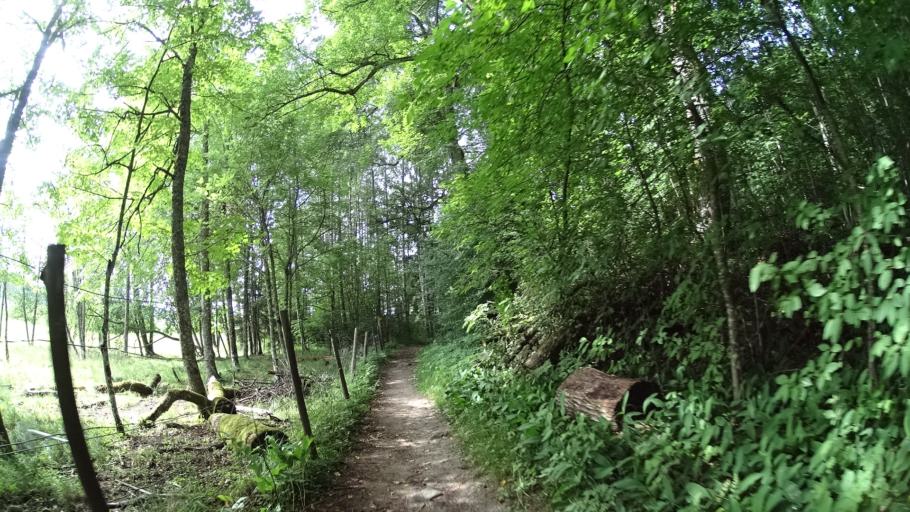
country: FI
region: Uusimaa
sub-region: Helsinki
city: Espoo
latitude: 60.1779
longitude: 24.5724
